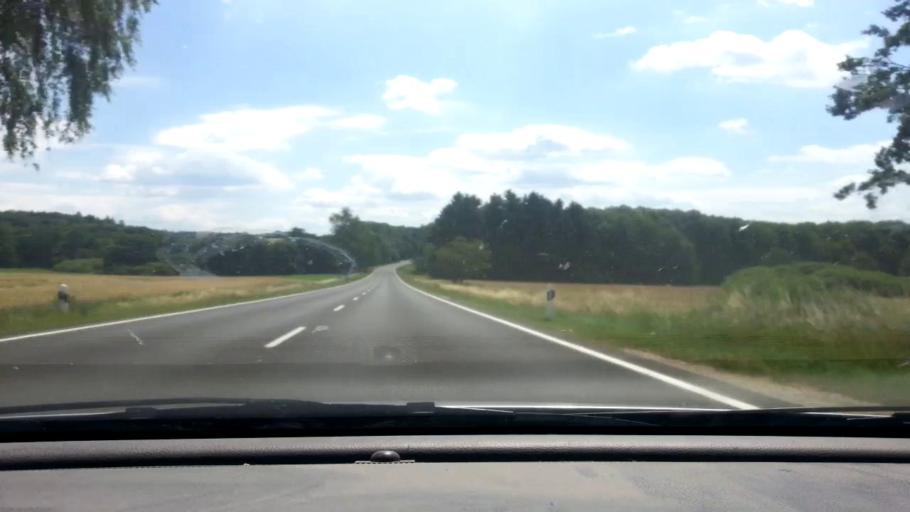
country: DE
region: Bavaria
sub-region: Upper Palatinate
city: Kastl
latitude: 49.8585
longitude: 11.9639
